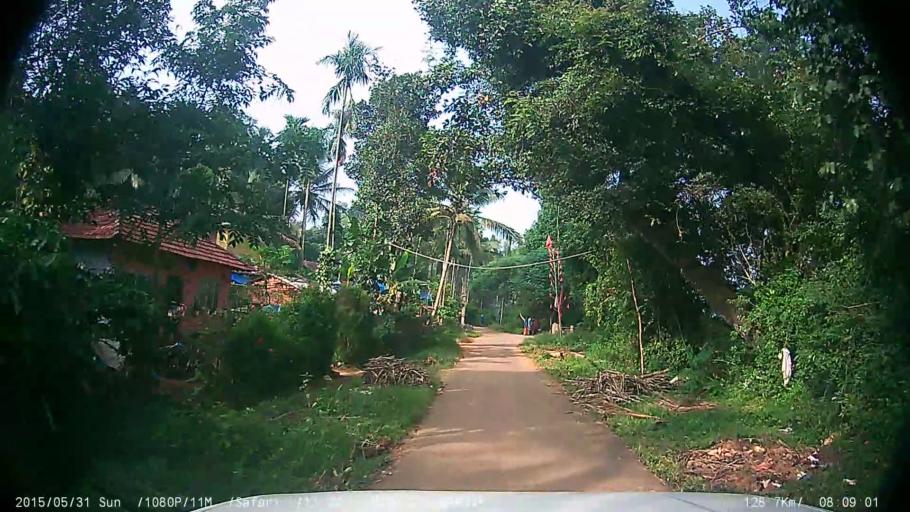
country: IN
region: Kerala
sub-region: Wayanad
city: Kalpetta
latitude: 11.6397
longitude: 76.0225
